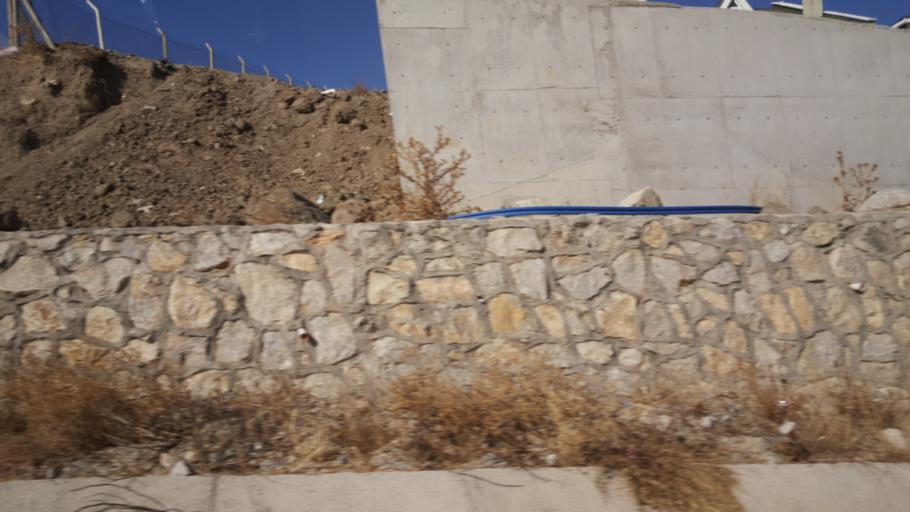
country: TR
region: Ankara
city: Ikizce
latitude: 39.5432
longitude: 32.6433
